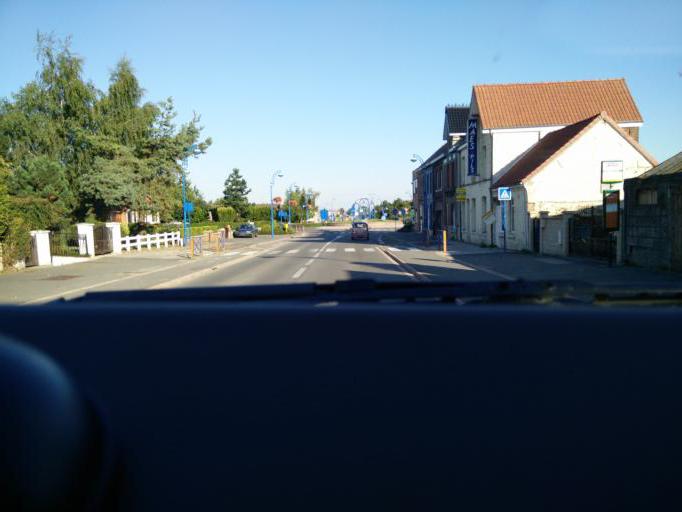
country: FR
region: Nord-Pas-de-Calais
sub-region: Departement du Pas-de-Calais
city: Noyelles-les-Vermelles
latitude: 50.4858
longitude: 2.7221
